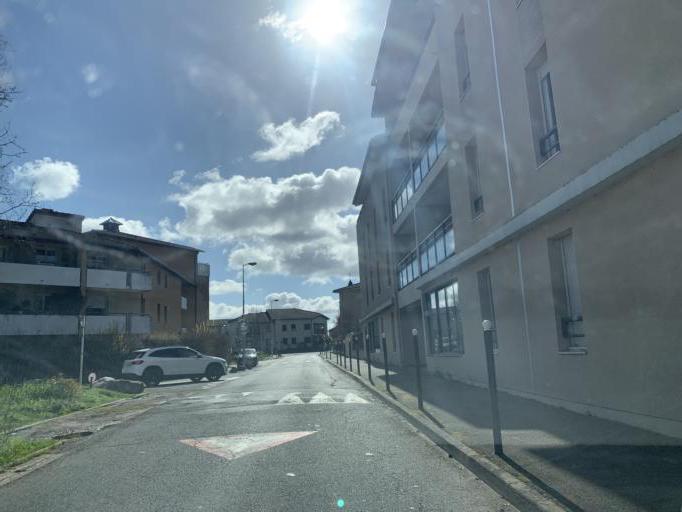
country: FR
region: Rhone-Alpes
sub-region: Departement de l'Ain
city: Saint-Andre-de-Corcy
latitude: 45.9493
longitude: 4.9852
